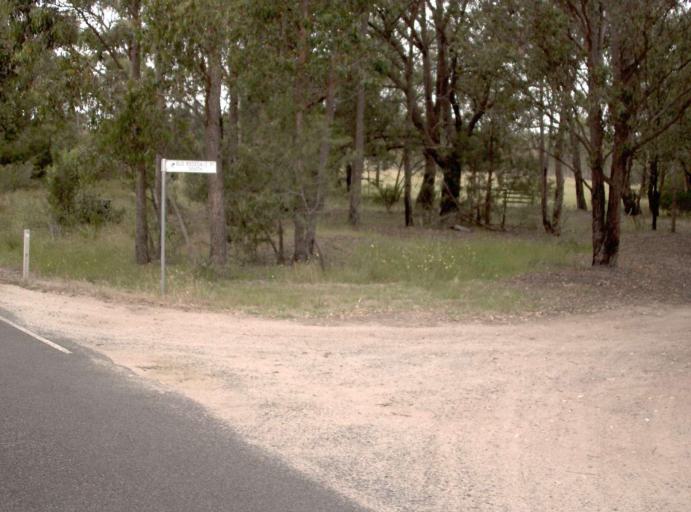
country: AU
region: Victoria
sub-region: Latrobe
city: Traralgon
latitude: -38.5082
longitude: 146.8470
